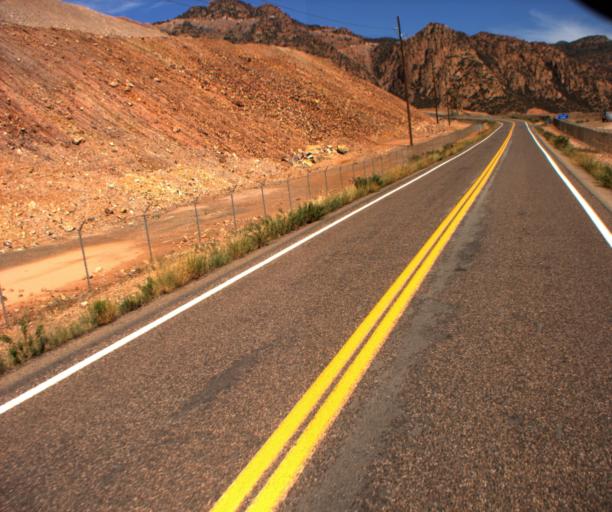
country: US
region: Arizona
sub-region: Greenlee County
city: Morenci
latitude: 33.1253
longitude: -109.3683
